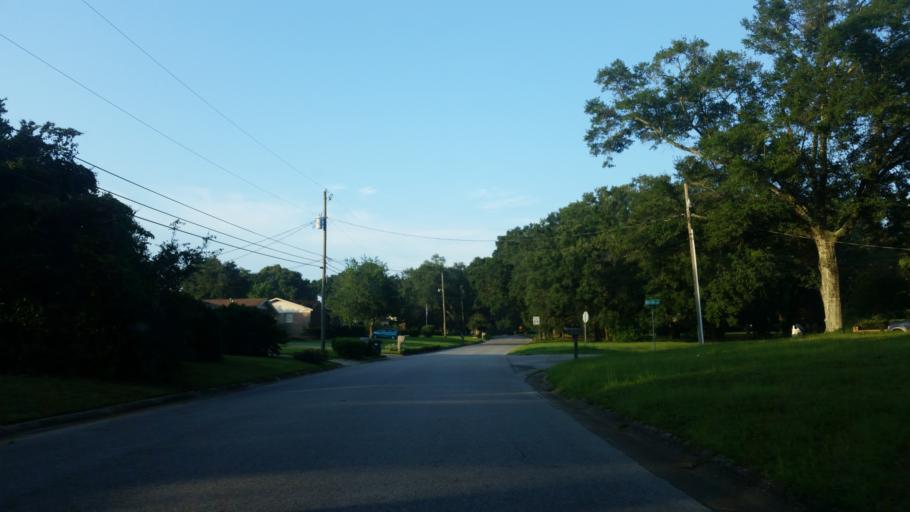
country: US
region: Florida
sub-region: Escambia County
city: Brent
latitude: 30.4900
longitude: -87.2389
